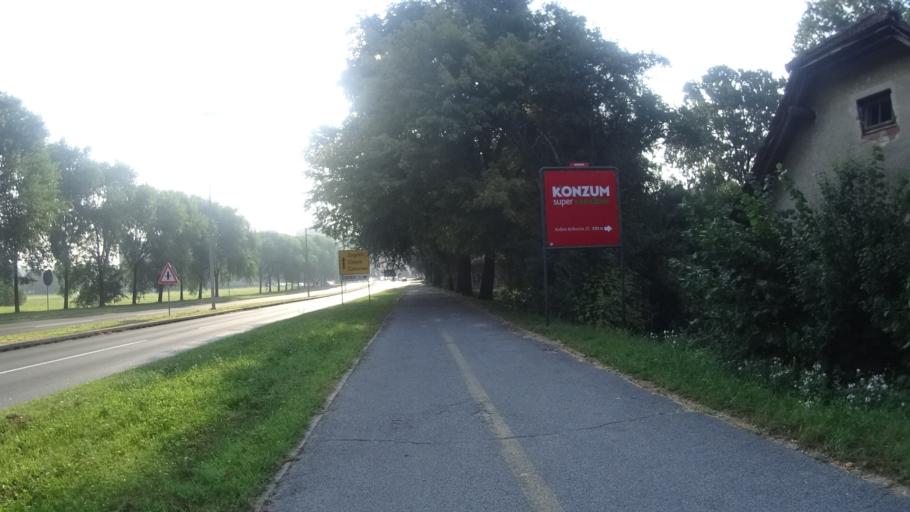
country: HR
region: Varazdinska
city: Varazdin
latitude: 46.3156
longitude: 16.3414
